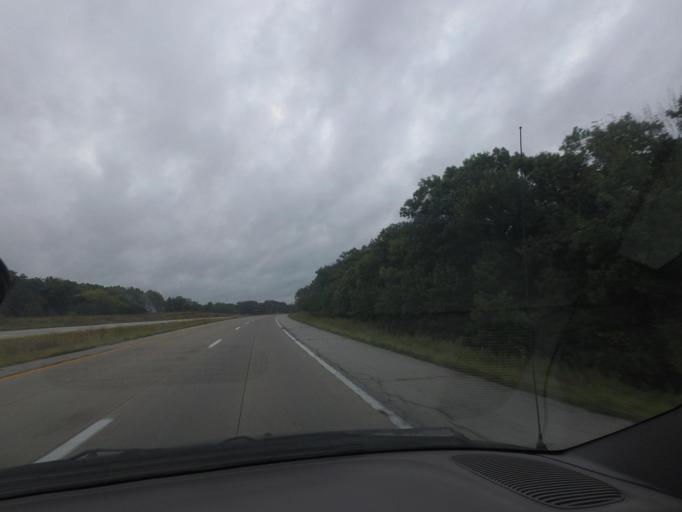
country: US
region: Missouri
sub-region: Shelby County
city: Shelbina
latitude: 39.6731
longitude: -91.8912
